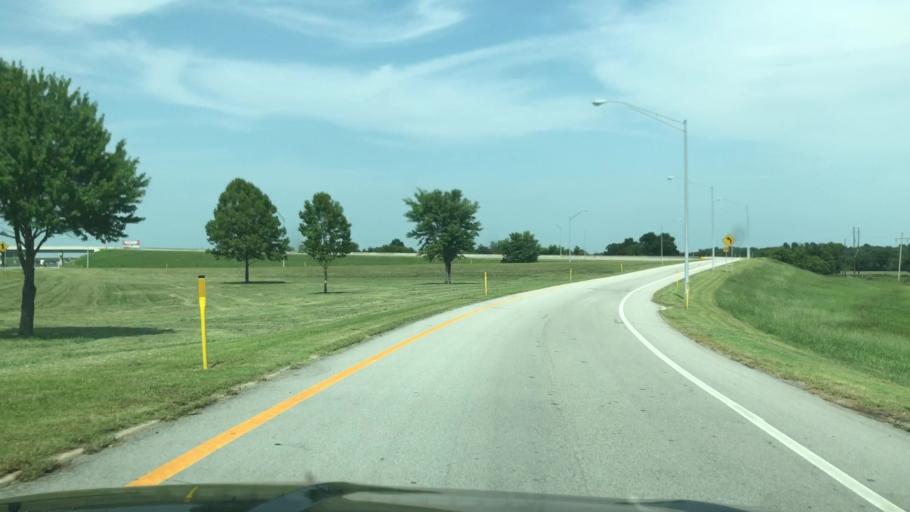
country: US
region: Oklahoma
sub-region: Ottawa County
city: Miami
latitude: 36.8627
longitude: -94.8508
